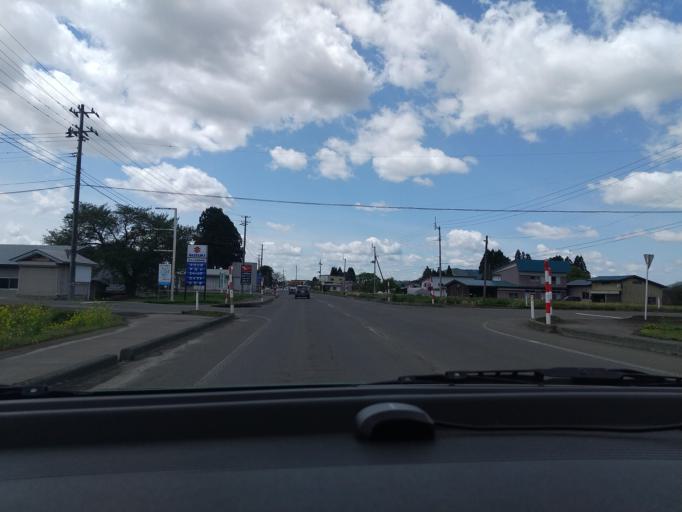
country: JP
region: Akita
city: Kakunodatemachi
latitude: 39.5743
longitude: 140.5637
